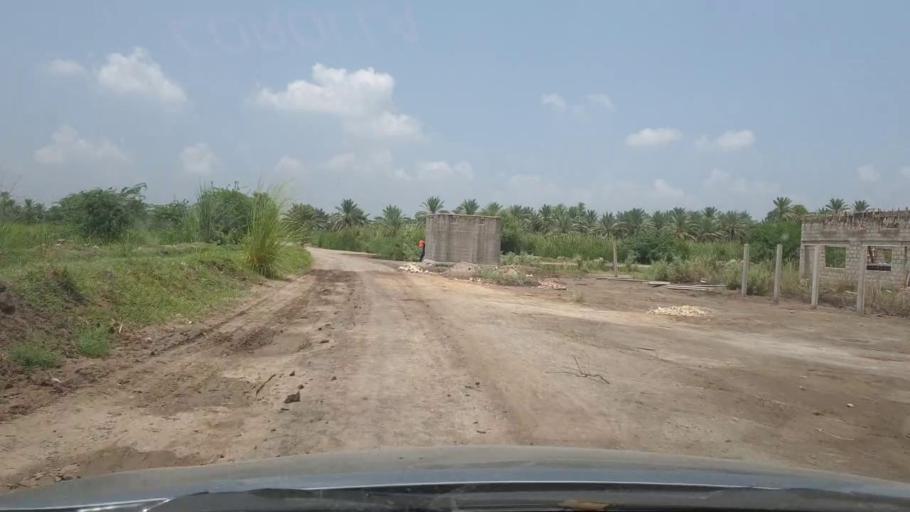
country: PK
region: Sindh
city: Khairpur
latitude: 27.4679
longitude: 68.7372
